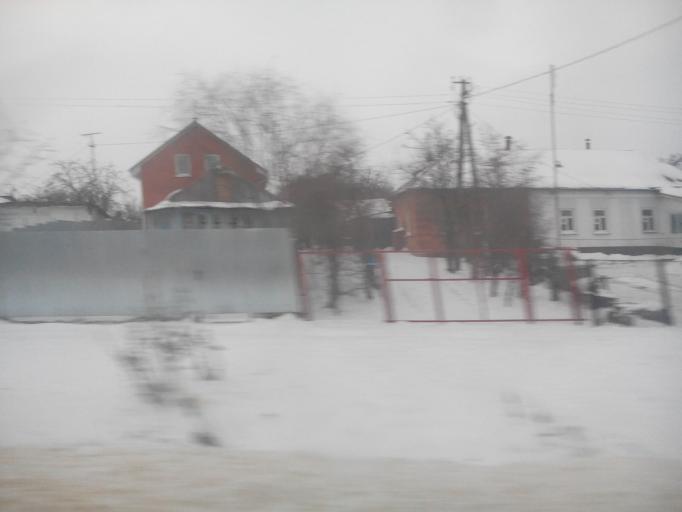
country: RU
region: Tula
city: Plavsk
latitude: 53.7937
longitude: 37.4277
